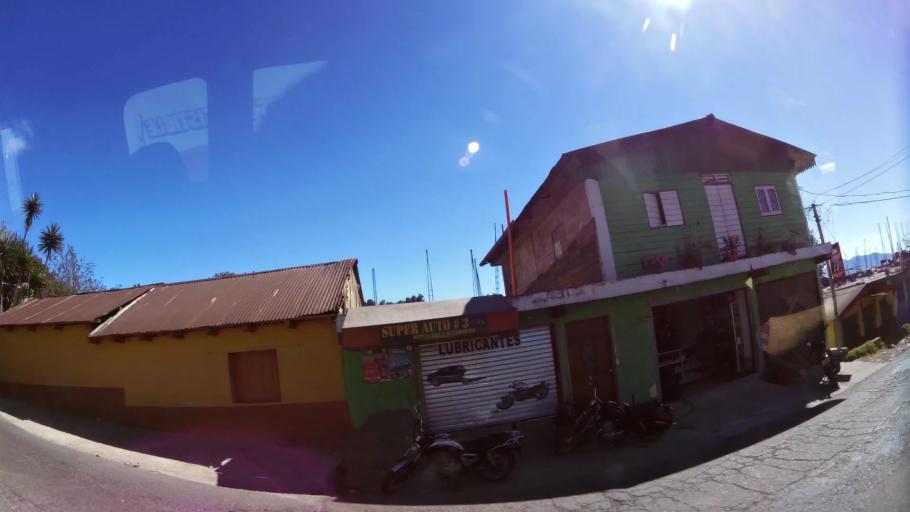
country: GT
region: Solola
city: Solola
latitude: 14.7778
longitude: -91.1814
